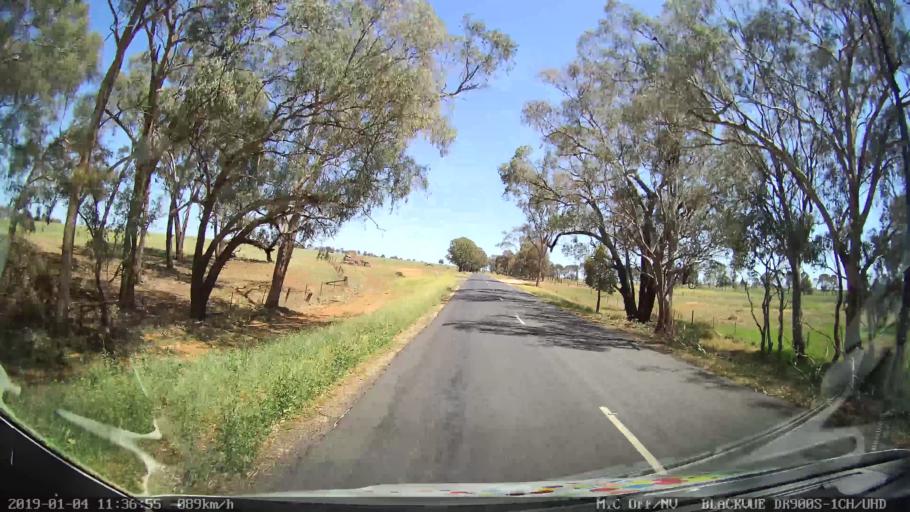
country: AU
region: New South Wales
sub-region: Cabonne
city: Molong
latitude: -33.0384
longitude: 148.8114
